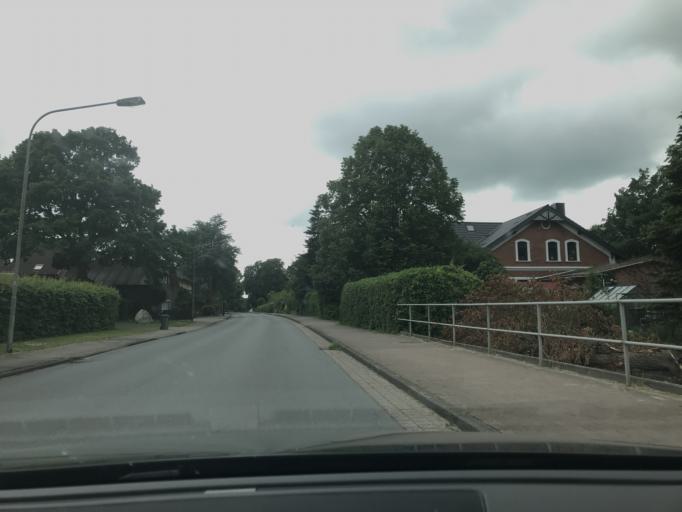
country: DE
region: Lower Saxony
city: Loxstedt
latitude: 53.4582
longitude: 8.6255
